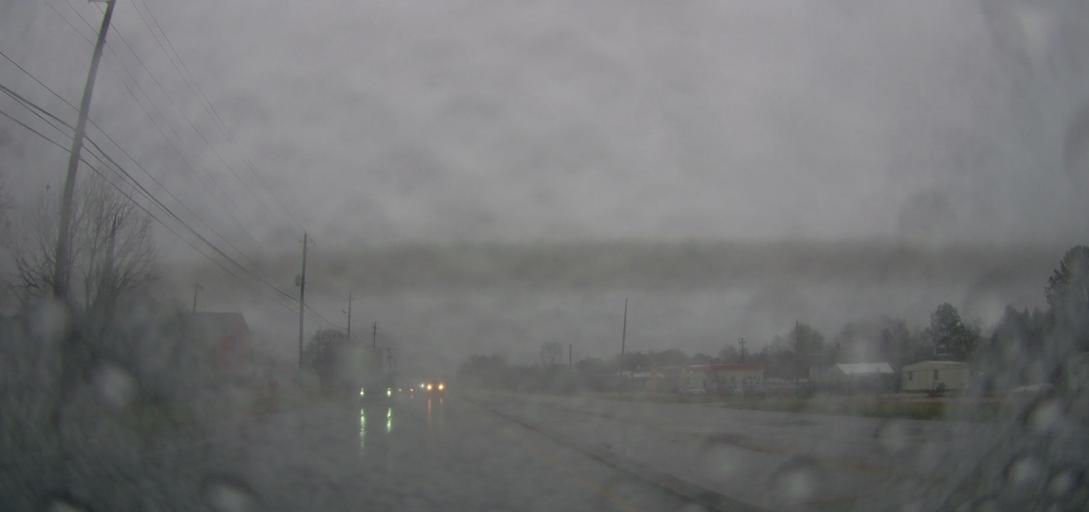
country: US
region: Alabama
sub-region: Autauga County
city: Prattville
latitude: 32.4007
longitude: -86.4003
